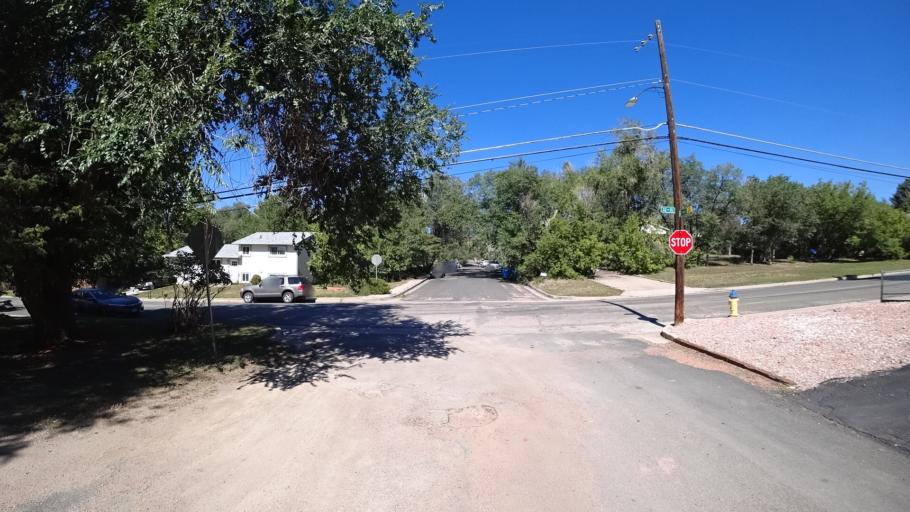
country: US
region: Colorado
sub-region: El Paso County
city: Manitou Springs
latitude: 38.8566
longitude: -104.8741
